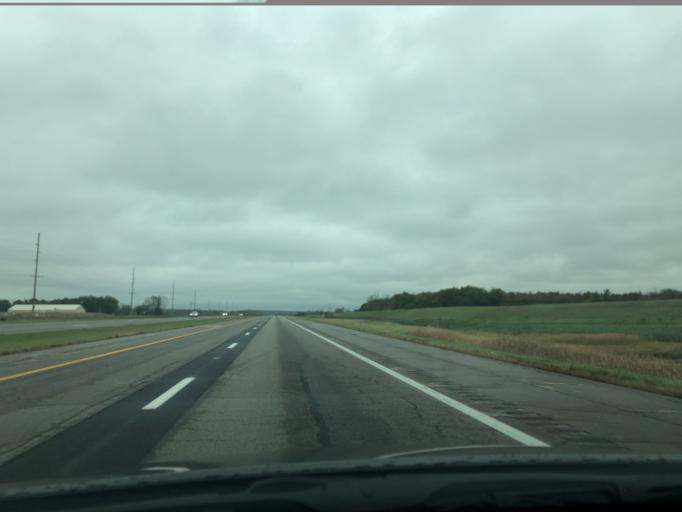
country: US
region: Ohio
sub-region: Champaign County
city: North Lewisburg
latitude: 40.2974
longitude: -83.5593
